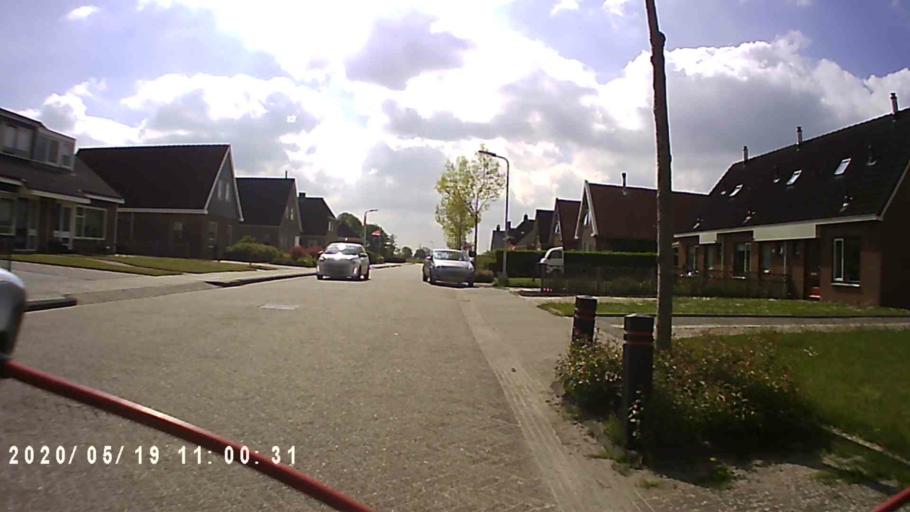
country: NL
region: Groningen
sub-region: Gemeente Zuidhorn
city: Grijpskerk
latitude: 53.3042
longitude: 6.2683
